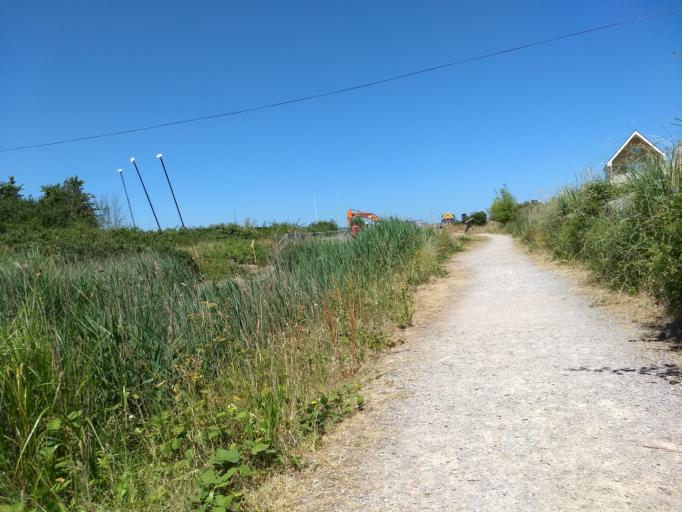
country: GB
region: England
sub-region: Isle of Wight
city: Seaview
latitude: 50.7222
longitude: -1.1186
